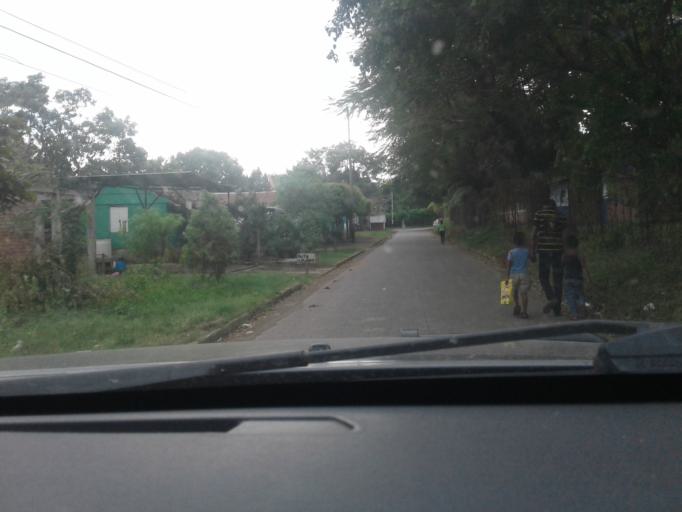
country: NI
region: Rivas
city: Buenos Aires
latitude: 11.4817
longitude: -85.8347
